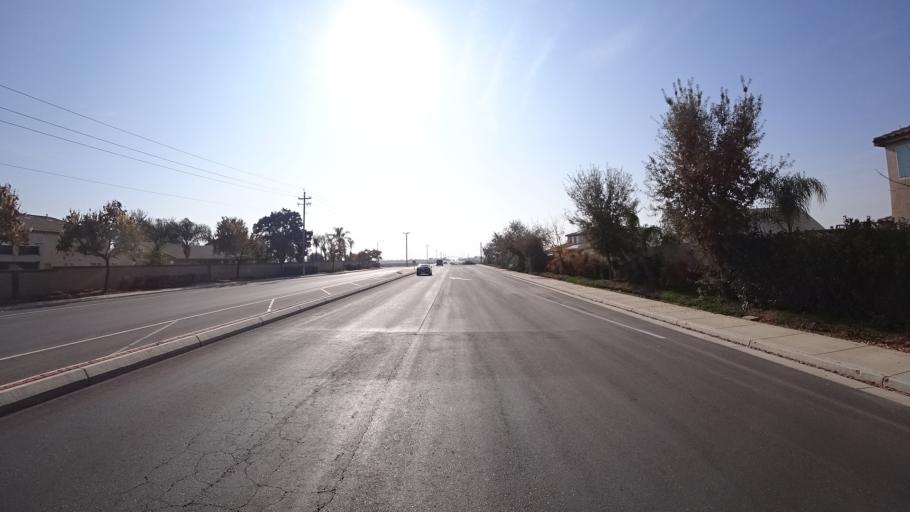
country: US
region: California
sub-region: Kern County
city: Greenacres
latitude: 35.3009
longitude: -119.1100
